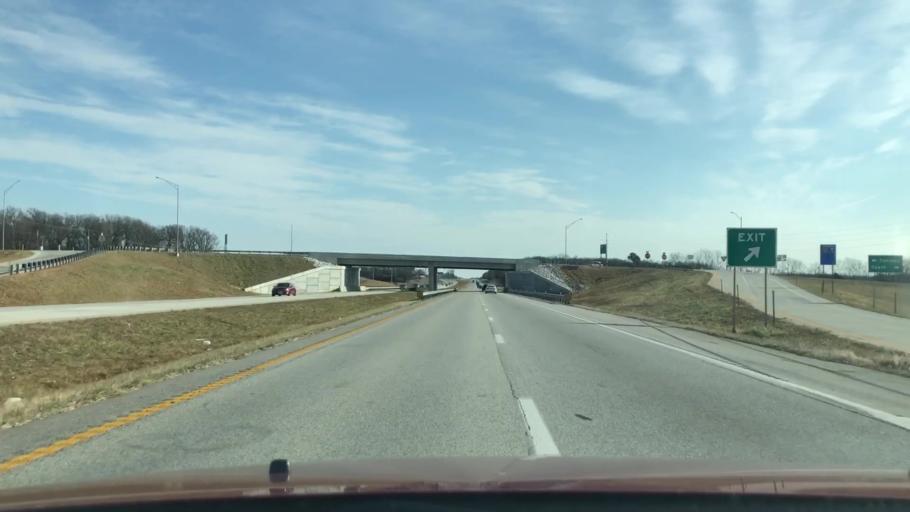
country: US
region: Missouri
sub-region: Christian County
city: Ozark
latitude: 37.1202
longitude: -93.1902
